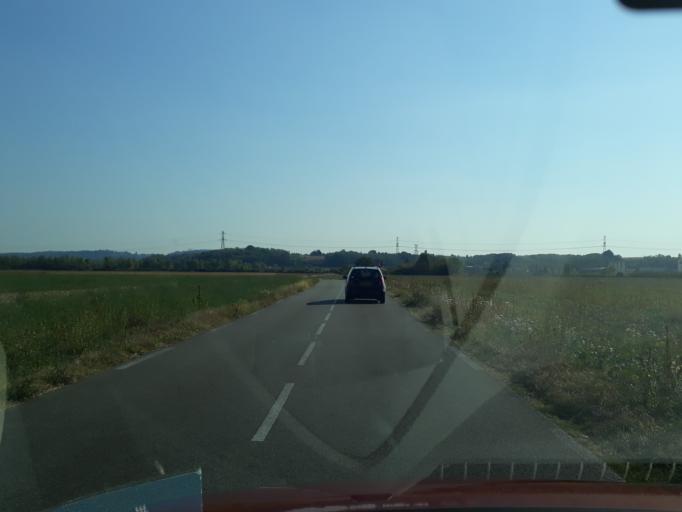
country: FR
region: Rhone-Alpes
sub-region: Departement du Rhone
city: Toussieu
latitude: 45.6778
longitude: 4.9832
